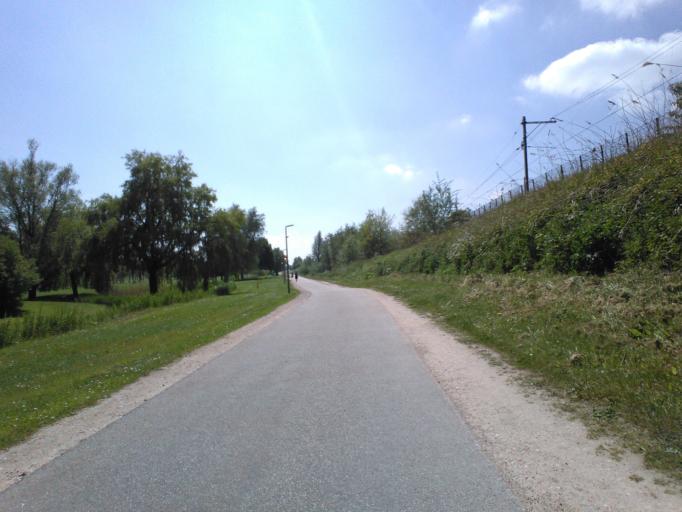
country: NL
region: South Holland
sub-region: Gemeente Sliedrecht
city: Sliedrecht
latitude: 51.8100
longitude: 4.7405
